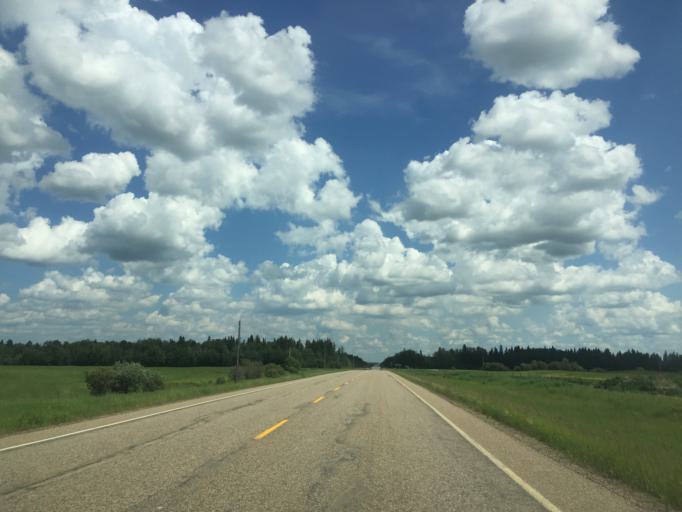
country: CA
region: Alberta
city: Athabasca
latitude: 54.3267
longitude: -113.2322
